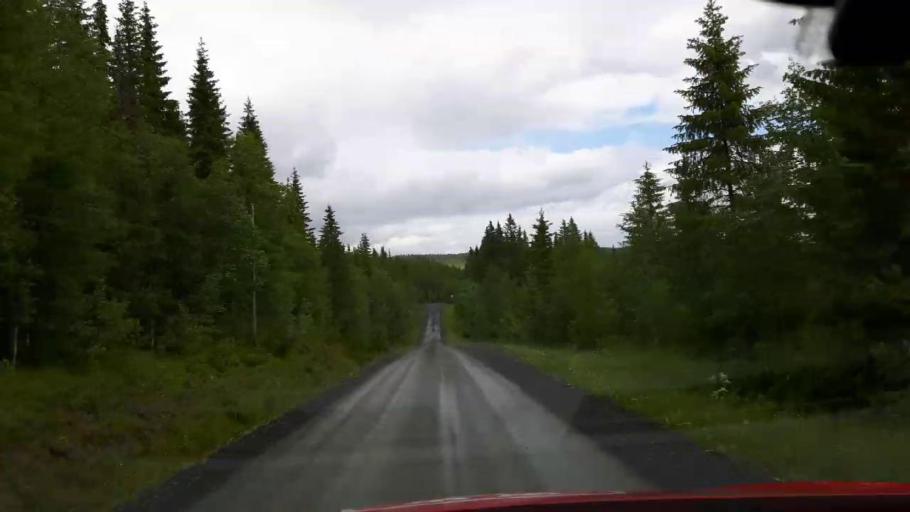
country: NO
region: Nord-Trondelag
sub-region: Lierne
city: Sandvika
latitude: 64.1597
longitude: 14.0337
